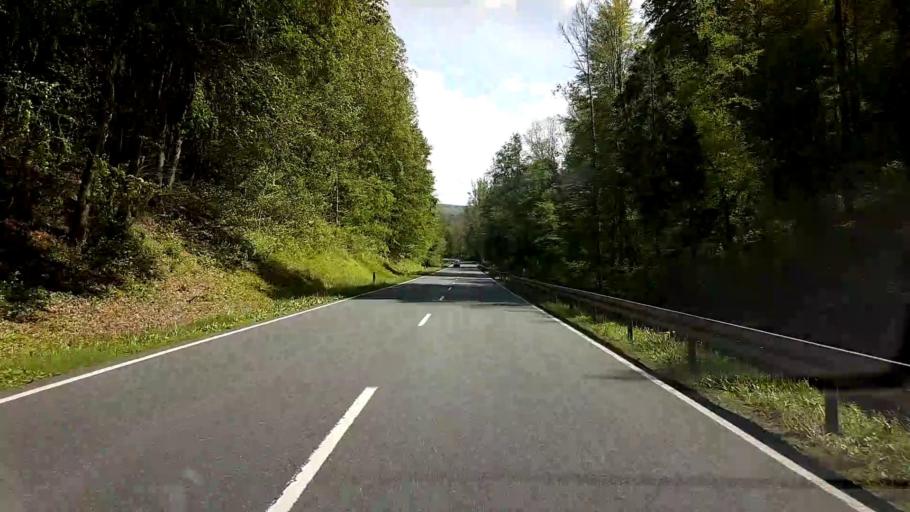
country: DE
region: Bavaria
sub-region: Upper Franconia
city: Ebermannstadt
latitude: 49.8034
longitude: 11.1661
